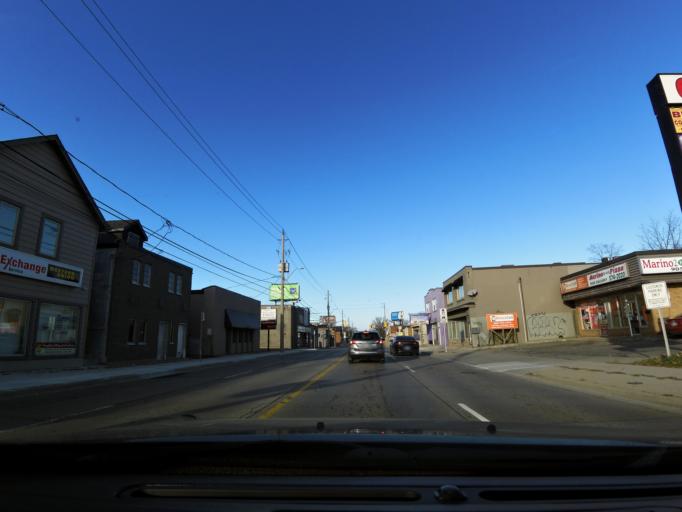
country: CA
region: Ontario
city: Hamilton
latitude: 43.2393
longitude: -79.8771
